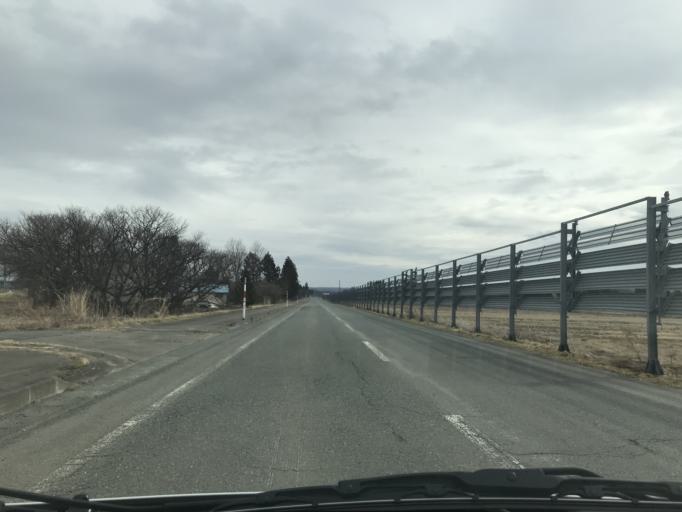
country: JP
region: Iwate
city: Hanamaki
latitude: 39.3362
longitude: 140.9938
